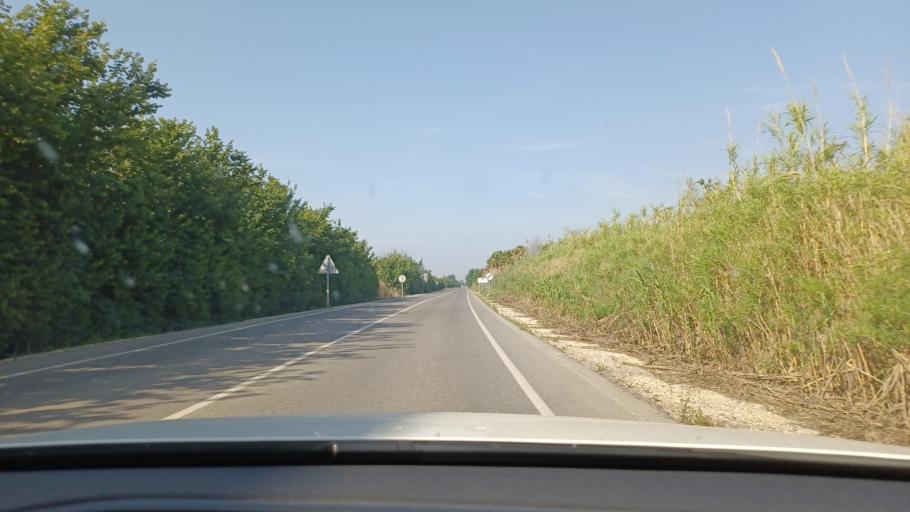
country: ES
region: Valencia
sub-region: Provincia de Alicante
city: Daya Vieja
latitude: 38.1584
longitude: -0.7042
